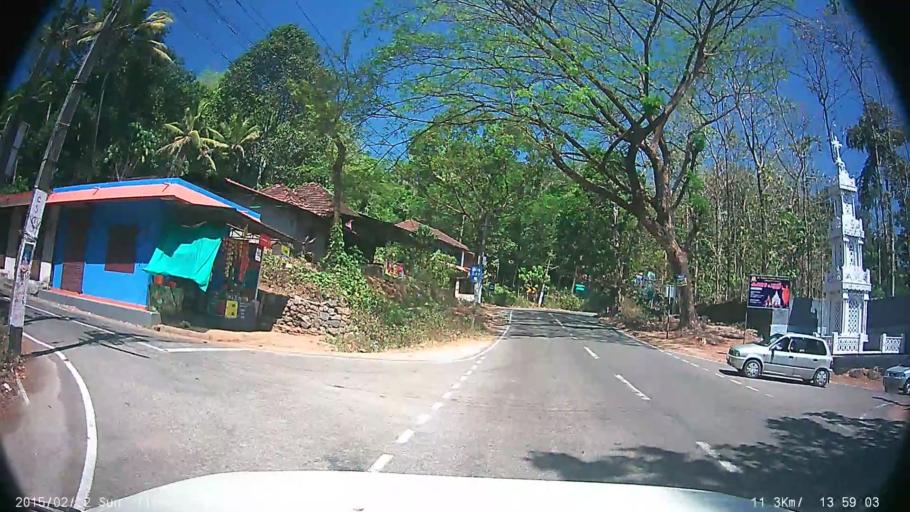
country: IN
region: Kerala
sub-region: Kottayam
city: Kottayam
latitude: 9.5385
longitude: 76.6773
